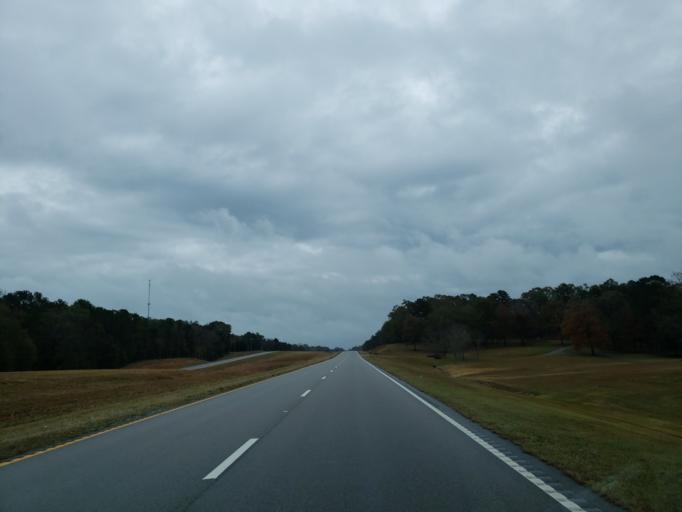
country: US
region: Mississippi
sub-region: Wayne County
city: Waynesboro
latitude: 31.6953
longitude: -88.7473
